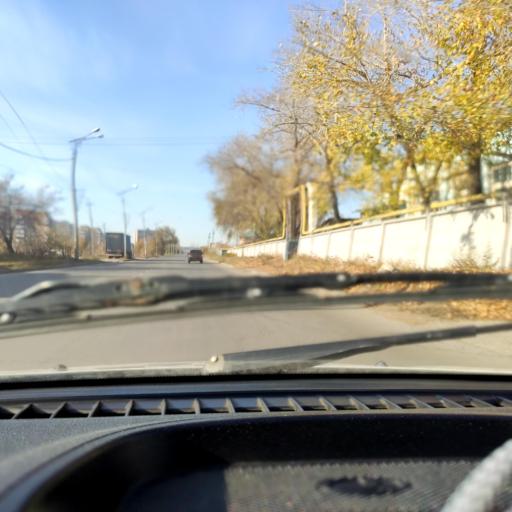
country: RU
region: Samara
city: Zhigulevsk
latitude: 53.4739
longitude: 49.5363
